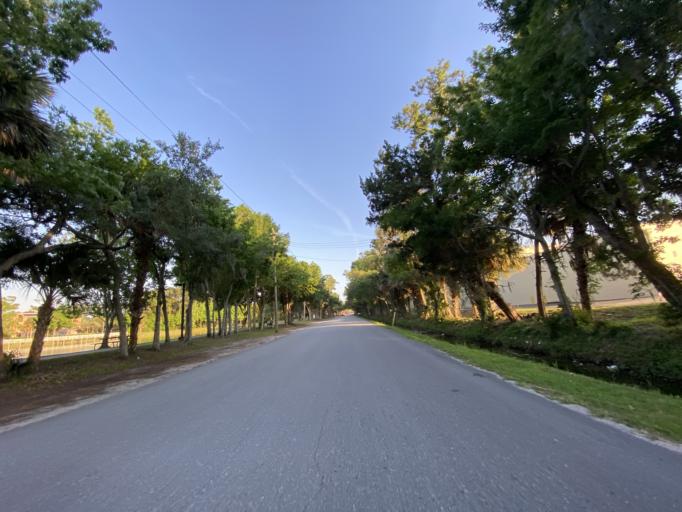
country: US
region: Florida
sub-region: Volusia County
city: Port Orange
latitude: 29.1317
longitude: -81.0050
